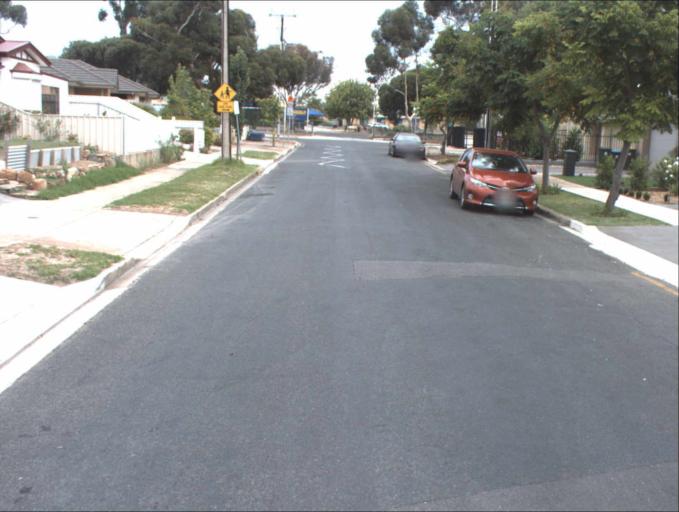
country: AU
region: South Australia
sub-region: Port Adelaide Enfield
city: Enfield
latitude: -34.8476
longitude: 138.6205
